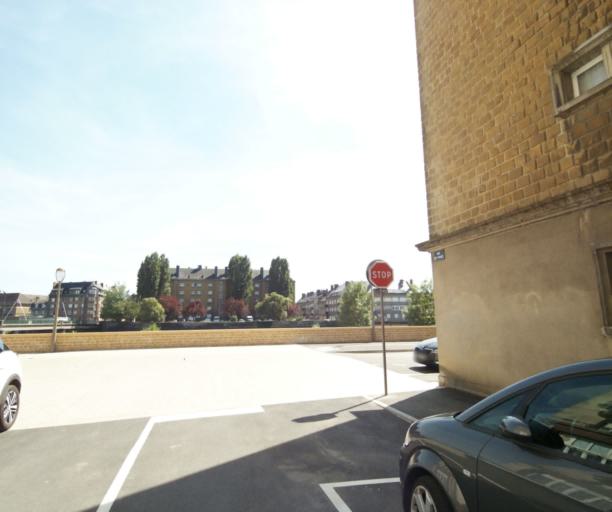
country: FR
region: Champagne-Ardenne
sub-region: Departement des Ardennes
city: Charleville-Mezieres
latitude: 49.7599
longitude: 4.7181
